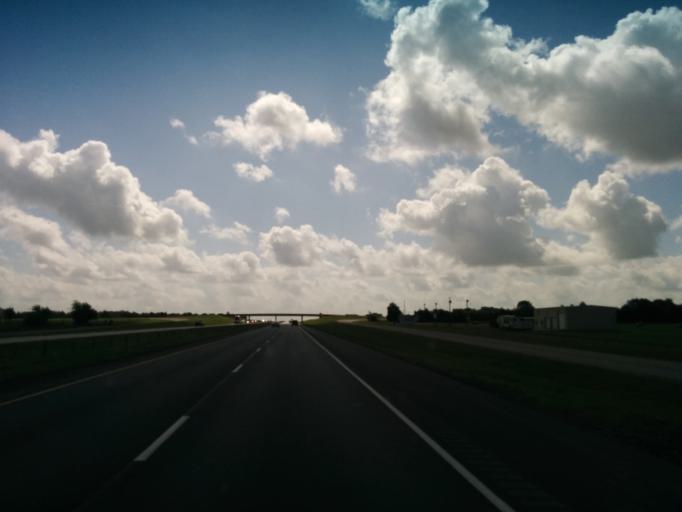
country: US
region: Texas
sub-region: Colorado County
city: Weimar
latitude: 29.6921
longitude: -96.7528
